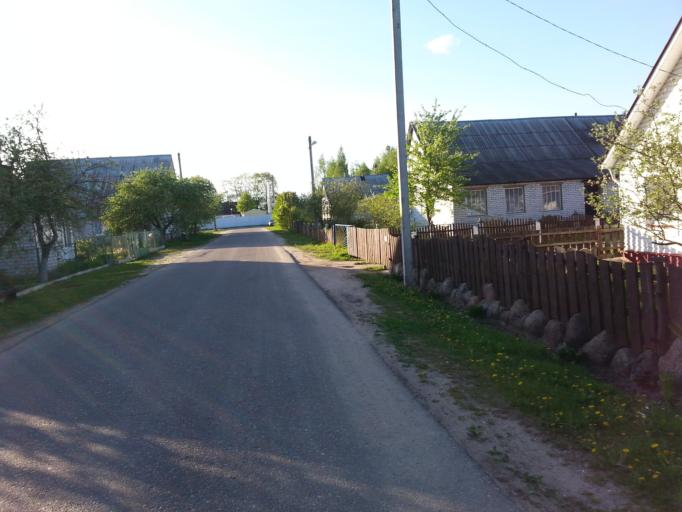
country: BY
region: Minsk
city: Narach
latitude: 54.9335
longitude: 26.6776
